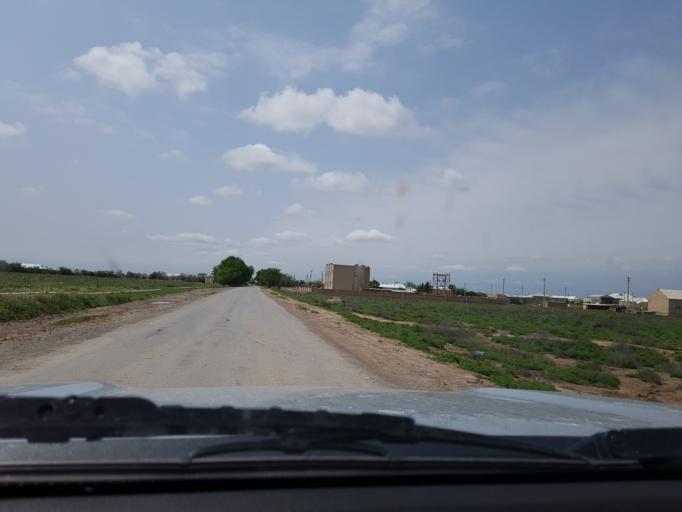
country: TM
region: Mary
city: Bayramaly
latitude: 37.6598
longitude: 62.1151
